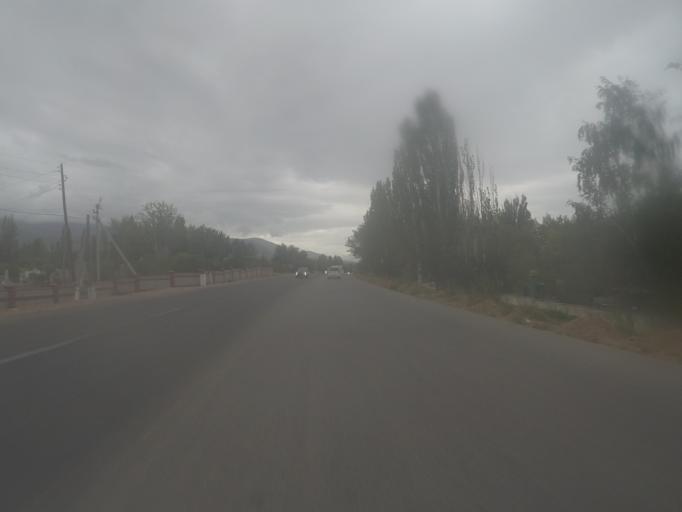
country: KG
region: Ysyk-Koel
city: Cholpon-Ata
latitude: 42.6852
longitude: 77.3396
